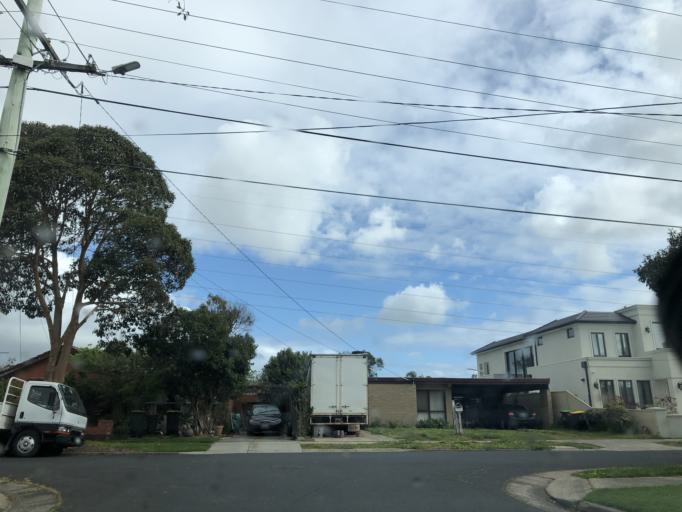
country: AU
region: Victoria
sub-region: Kingston
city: Clayton South
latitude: -37.9367
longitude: 145.1122
